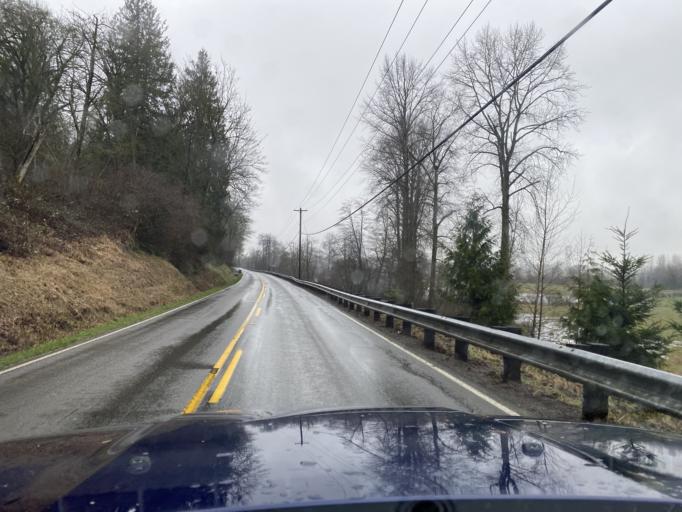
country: US
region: Washington
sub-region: King County
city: Duvall
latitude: 47.7967
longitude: -122.0009
